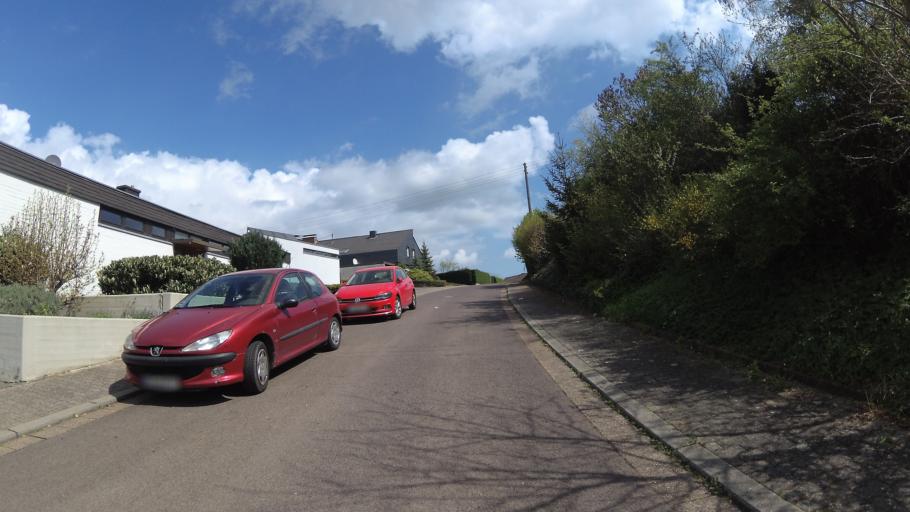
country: DE
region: Saarland
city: Wadern
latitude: 49.5296
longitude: 6.8747
